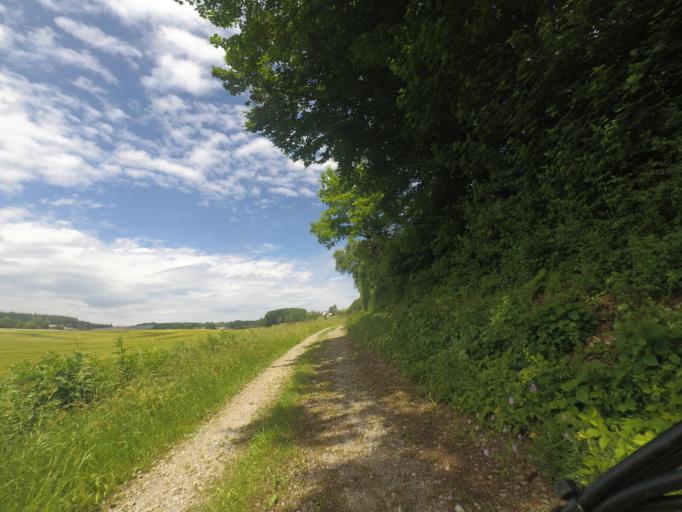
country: DE
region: Rheinland-Pfalz
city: Feusdorf
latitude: 50.3427
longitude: 6.6111
